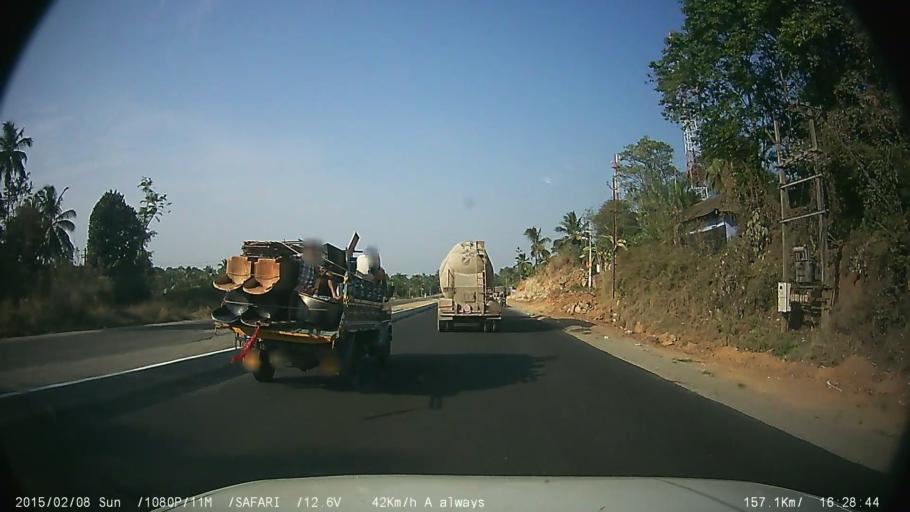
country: IN
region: Kerala
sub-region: Palakkad district
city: Palakkad
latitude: 10.6825
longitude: 76.5789
